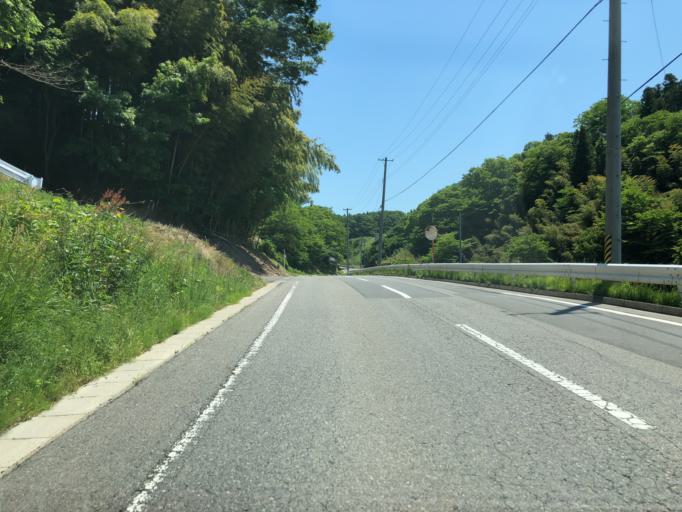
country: JP
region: Fukushima
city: Miharu
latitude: 37.4984
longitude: 140.4886
